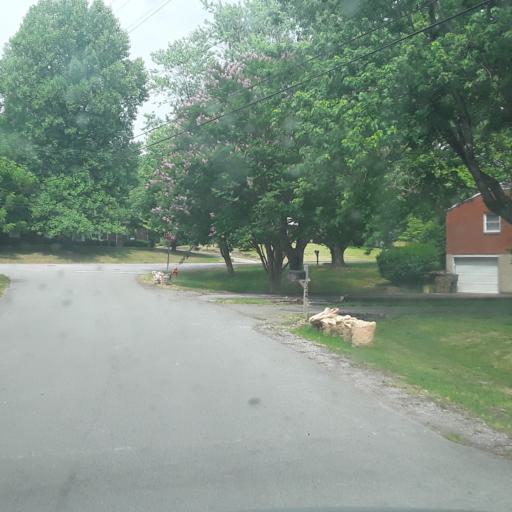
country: US
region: Tennessee
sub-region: Davidson County
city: Oak Hill
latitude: 36.0770
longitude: -86.7438
